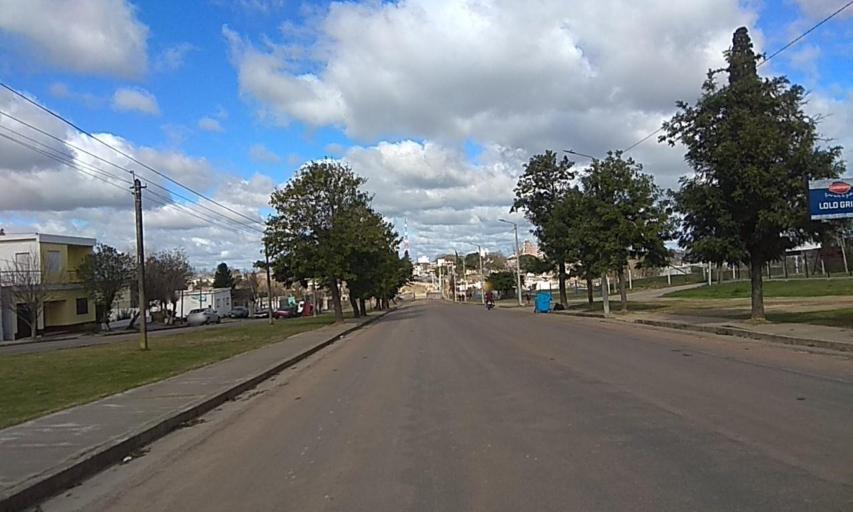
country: UY
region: Florida
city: Florida
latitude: -34.0875
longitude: -56.2224
